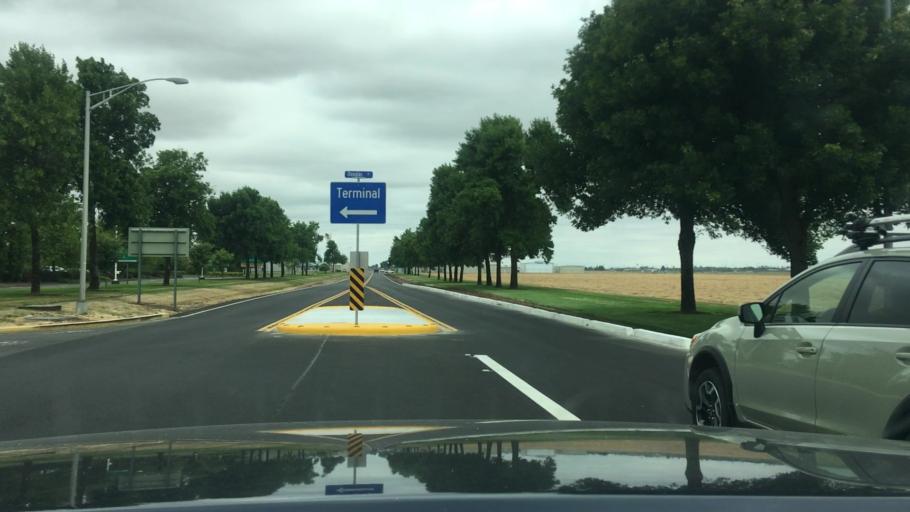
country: US
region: Oregon
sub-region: Lane County
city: Junction City
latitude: 44.1175
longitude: -123.2084
